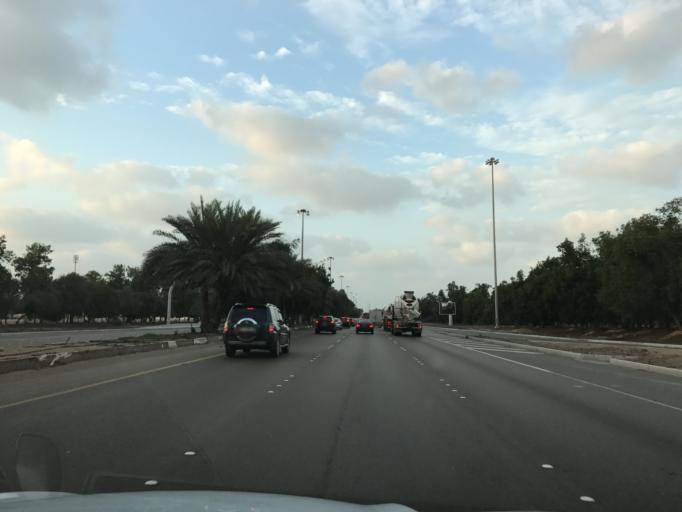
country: AE
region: Abu Dhabi
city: Abu Dhabi
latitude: 24.3975
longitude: 54.5238
